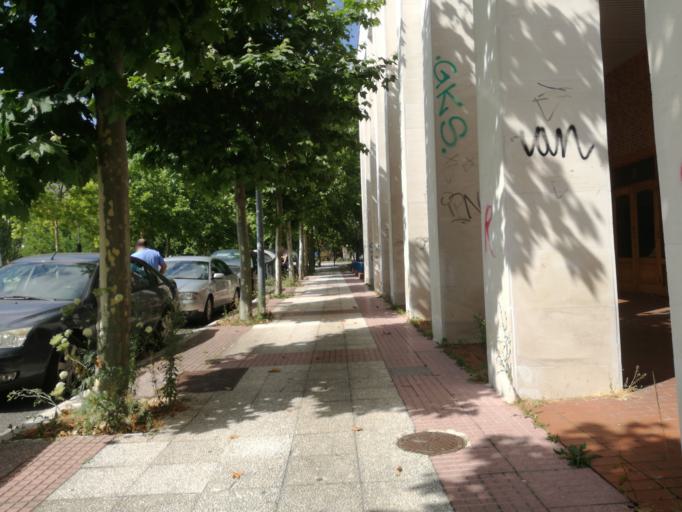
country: ES
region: Basque Country
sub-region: Provincia de Alava
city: Gasteiz / Vitoria
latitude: 42.8524
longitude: -2.6917
